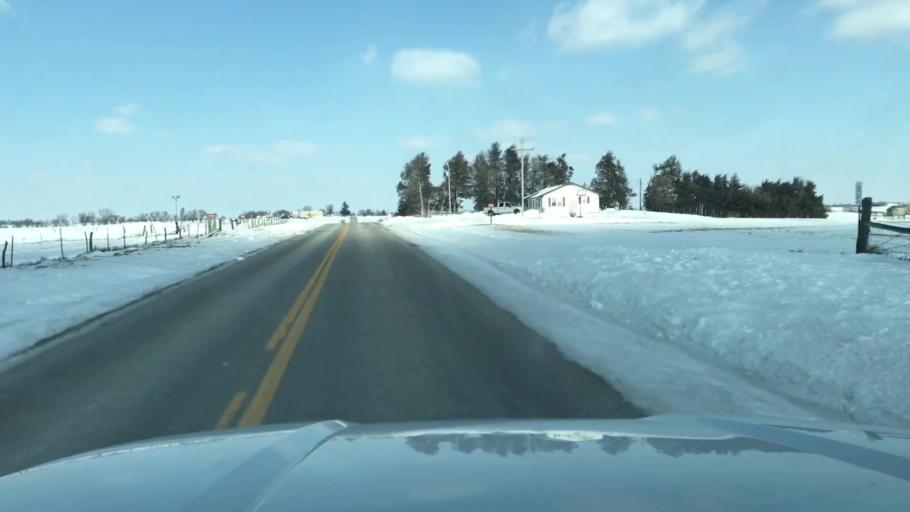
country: US
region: Missouri
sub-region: Nodaway County
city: Maryville
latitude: 40.3724
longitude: -94.7214
